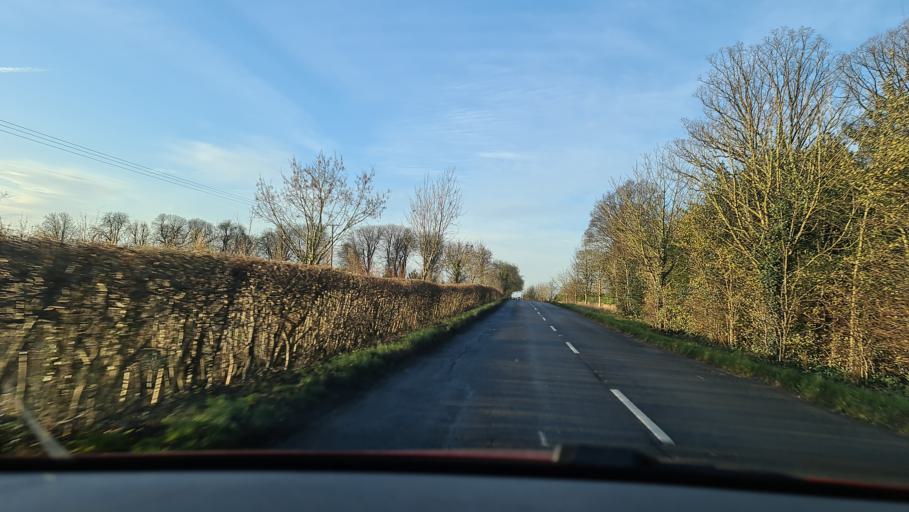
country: GB
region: England
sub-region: Buckinghamshire
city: Waddesdon
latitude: 51.8239
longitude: -0.9153
